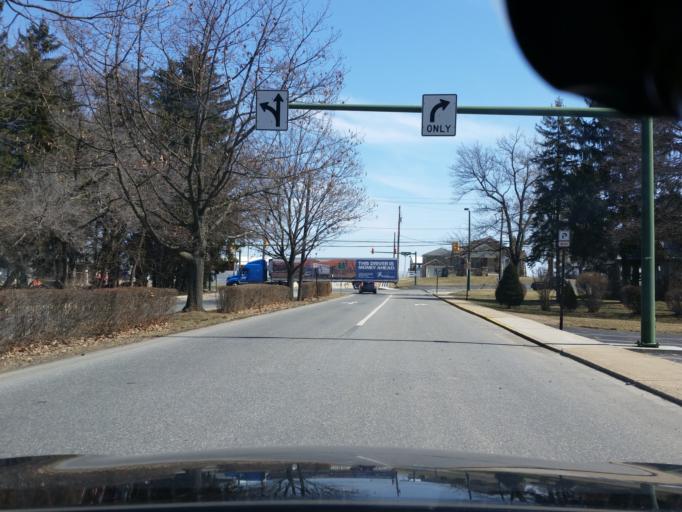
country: US
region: Pennsylvania
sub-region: Cumberland County
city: Carlisle
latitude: 40.2183
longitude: -77.1879
